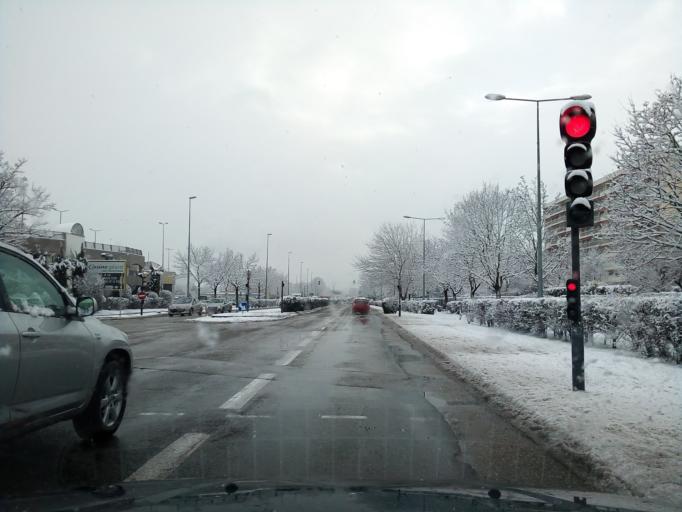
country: FR
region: Rhone-Alpes
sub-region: Departement de l'Isere
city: Corenc
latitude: 45.2051
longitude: 5.7643
